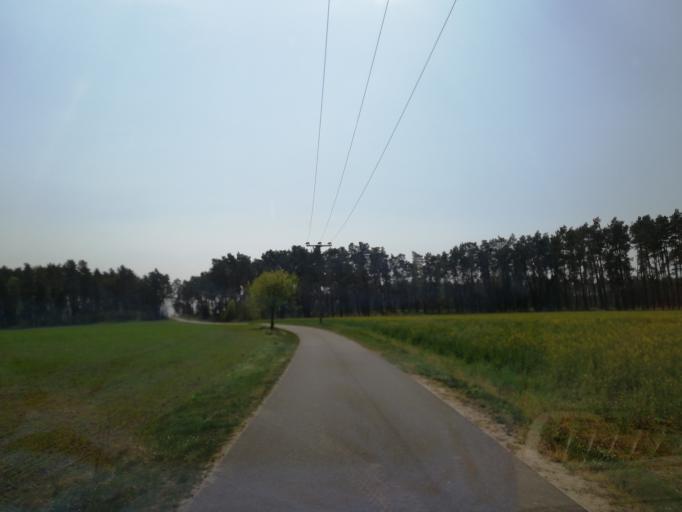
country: DE
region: Brandenburg
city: Bronkow
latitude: 51.6549
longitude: 13.8551
